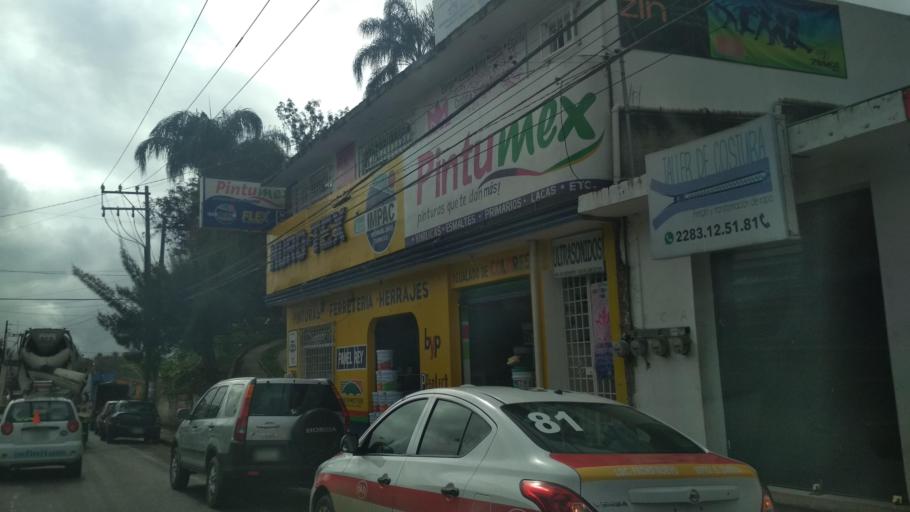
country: MX
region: Veracruz
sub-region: Emiliano Zapata
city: Las Trancas
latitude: 19.5056
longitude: -96.8631
